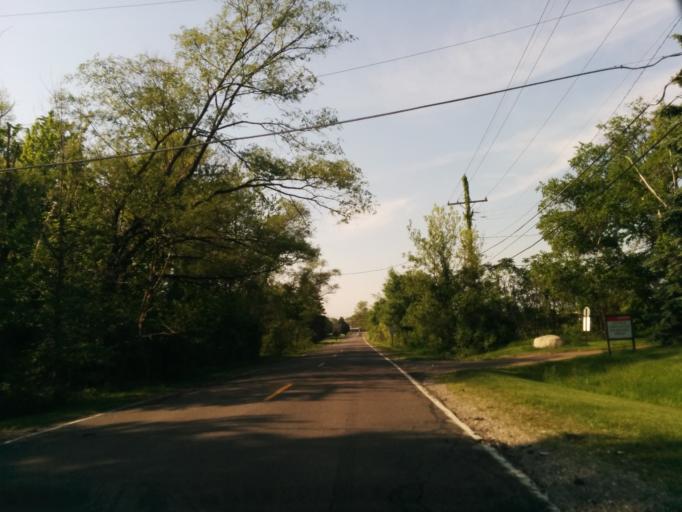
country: US
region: Michigan
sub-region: Oakland County
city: Novi
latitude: 42.4786
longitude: -83.4456
